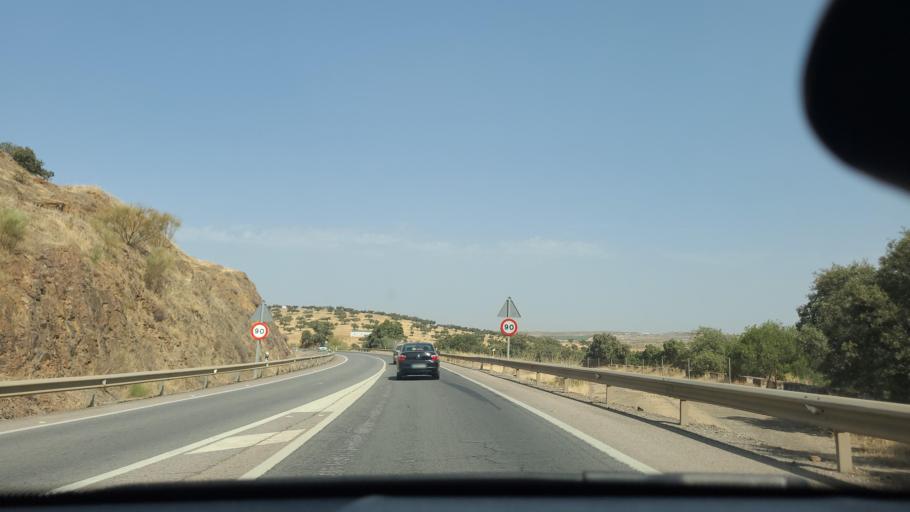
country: ES
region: Extremadura
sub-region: Provincia de Badajoz
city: Zafra
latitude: 38.4670
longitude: -6.4425
